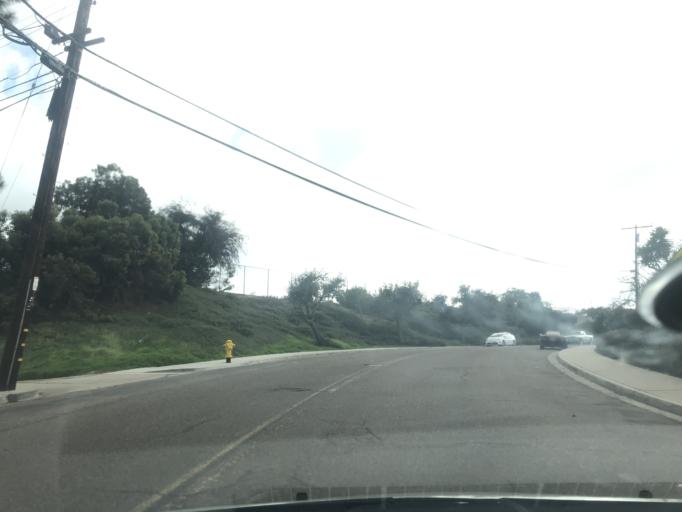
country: US
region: California
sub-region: San Diego County
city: San Diego
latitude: 32.7940
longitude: -117.1249
